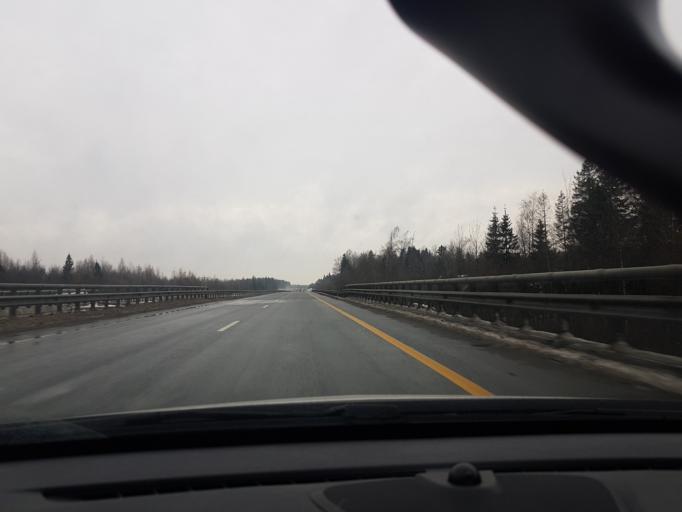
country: RU
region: Moskovskaya
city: Novopetrovskoye
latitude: 55.9817
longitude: 36.4152
